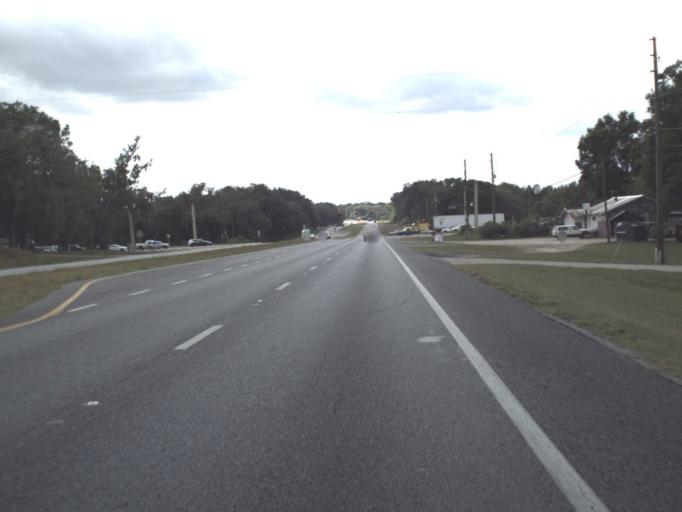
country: US
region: Florida
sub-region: Marion County
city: Belleview
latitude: 29.0312
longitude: -82.0450
